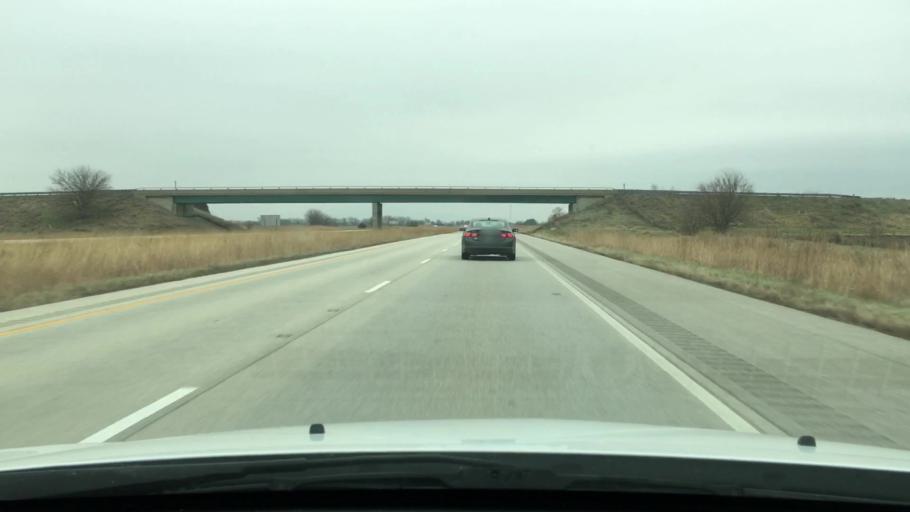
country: US
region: Illinois
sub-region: Sangamon County
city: New Berlin
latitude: 39.7404
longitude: -89.9023
